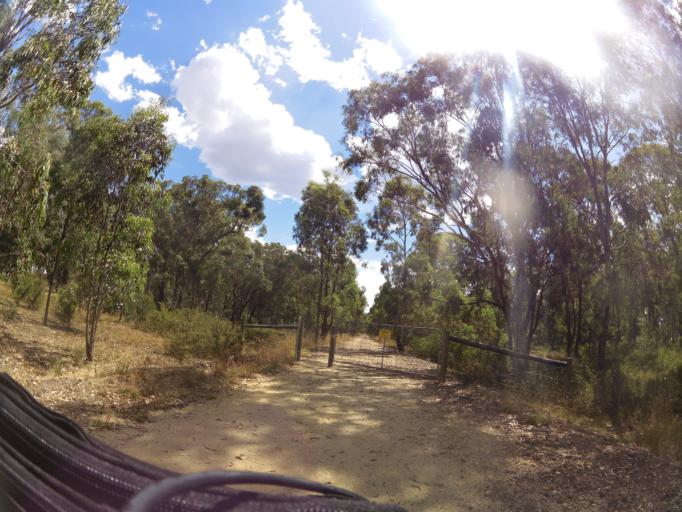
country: AU
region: Victoria
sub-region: Wellington
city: Heyfield
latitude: -37.9827
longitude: 146.7290
